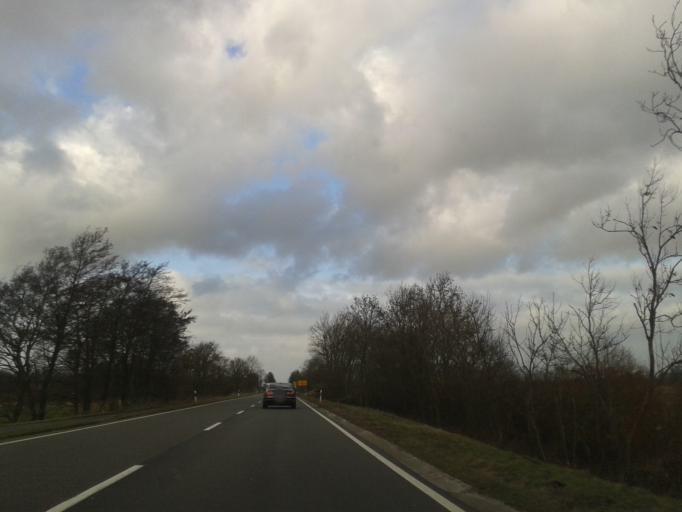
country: DE
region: Lower Saxony
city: Upgant-Schott
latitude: 53.4933
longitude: 7.3063
